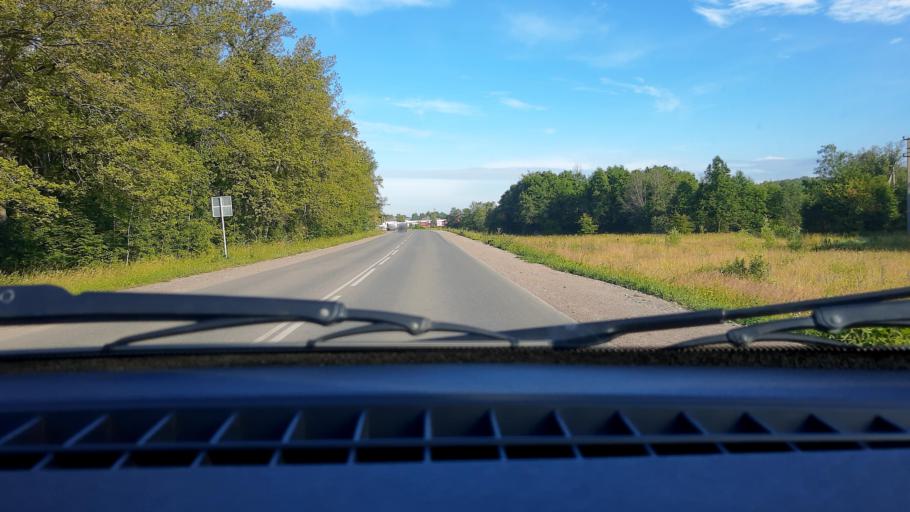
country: RU
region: Bashkortostan
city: Mikhaylovka
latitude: 54.8073
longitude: 55.8206
